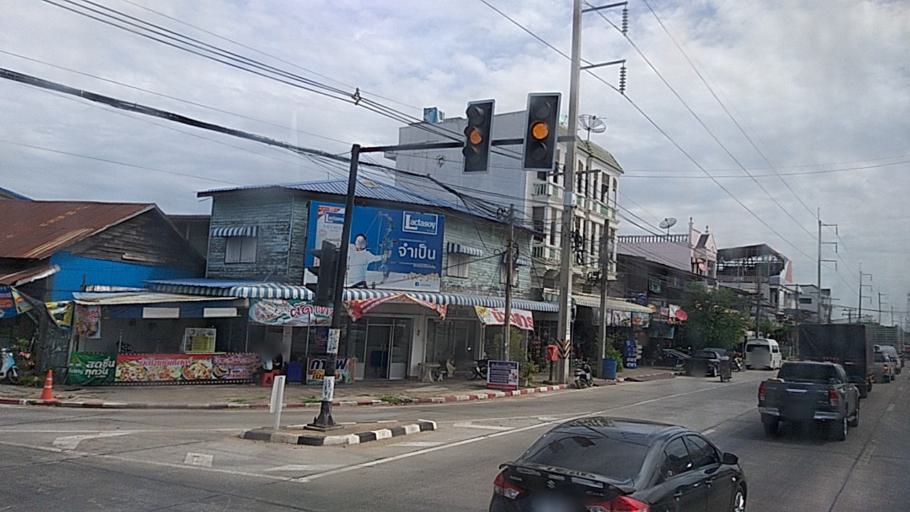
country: TH
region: Maha Sarakham
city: Chiang Yuen
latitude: 16.4100
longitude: 103.0980
